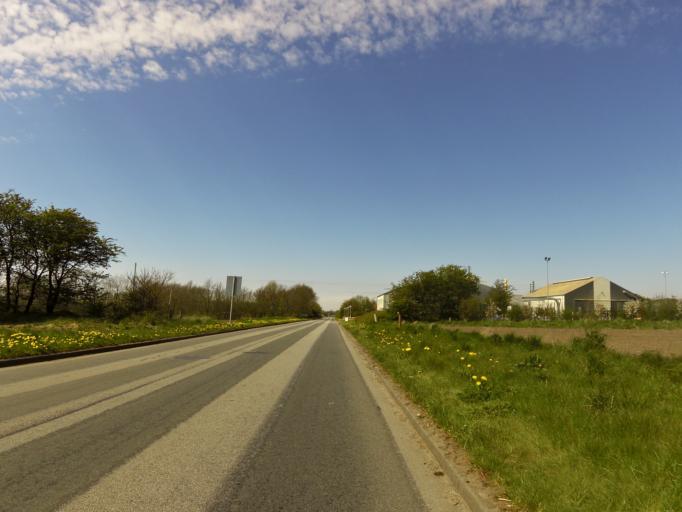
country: DK
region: South Denmark
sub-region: Tonder Kommune
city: Sherrebek
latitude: 55.1571
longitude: 8.7824
